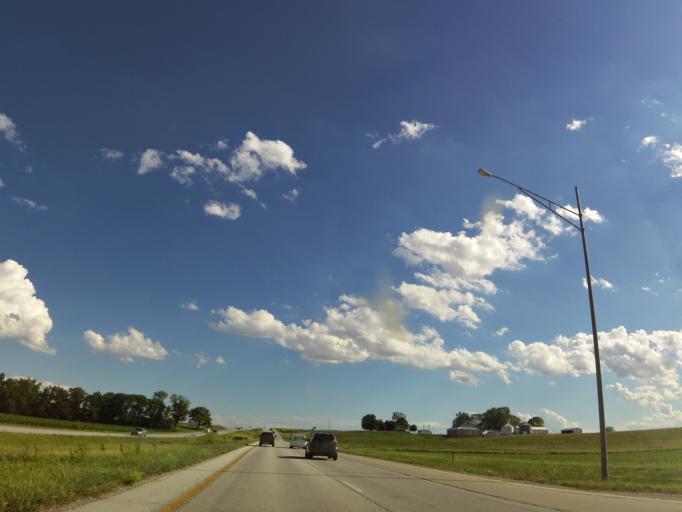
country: US
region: Illinois
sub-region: Adams County
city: Quincy
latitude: 39.9137
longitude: -91.5246
